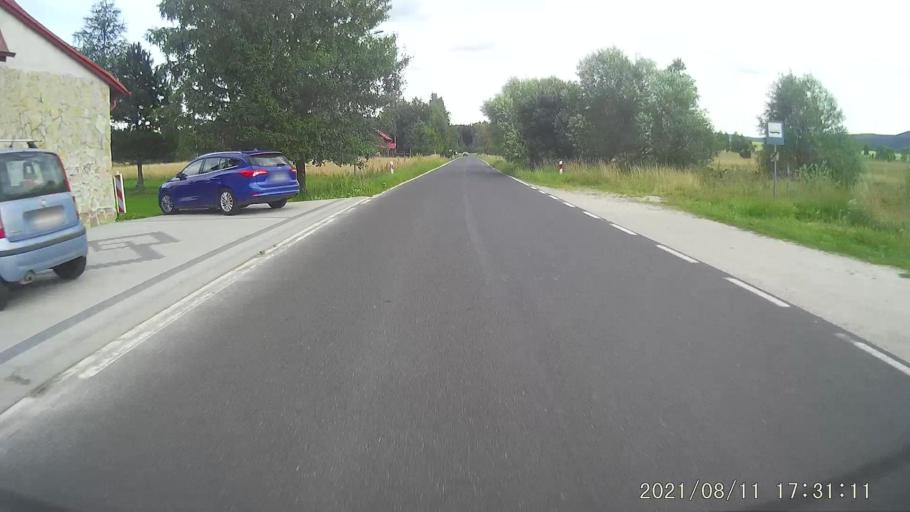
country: PL
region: Lower Silesian Voivodeship
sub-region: Powiat klodzki
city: Szczytna
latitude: 50.2992
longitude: 16.4586
